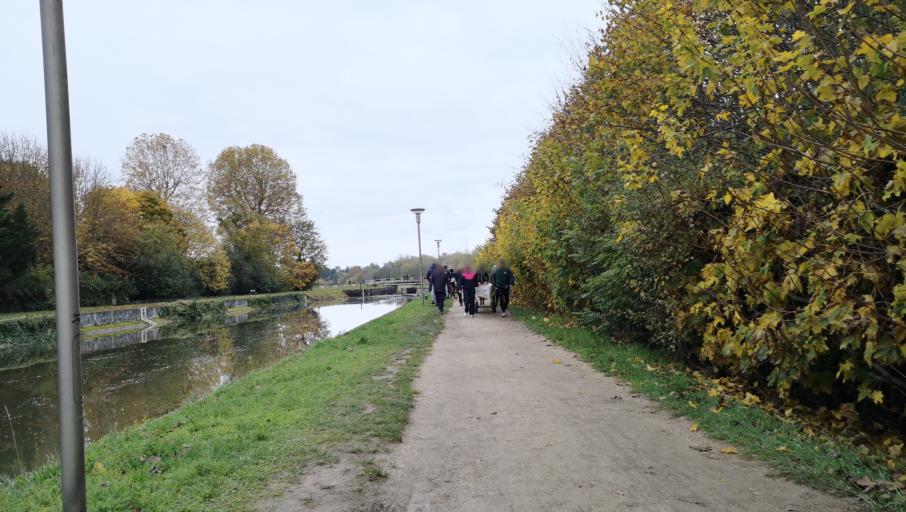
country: FR
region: Centre
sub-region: Departement du Loiret
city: Saint-Jean-de-Braye
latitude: 47.8999
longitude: 1.9859
